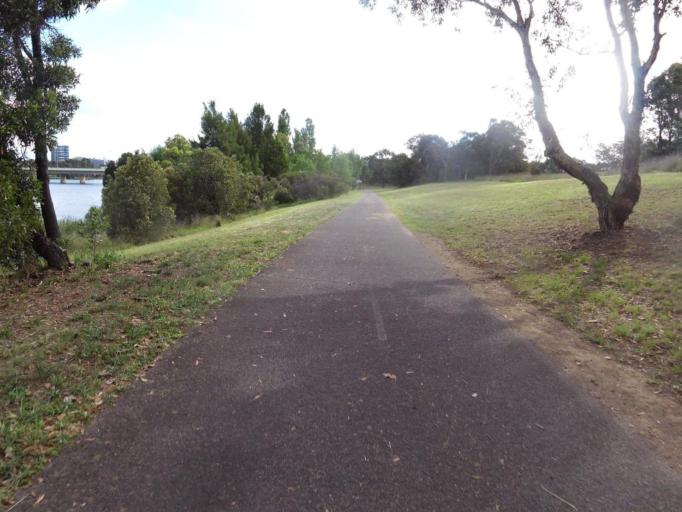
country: AU
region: Australian Capital Territory
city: Belconnen
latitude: -35.2262
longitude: 149.0779
